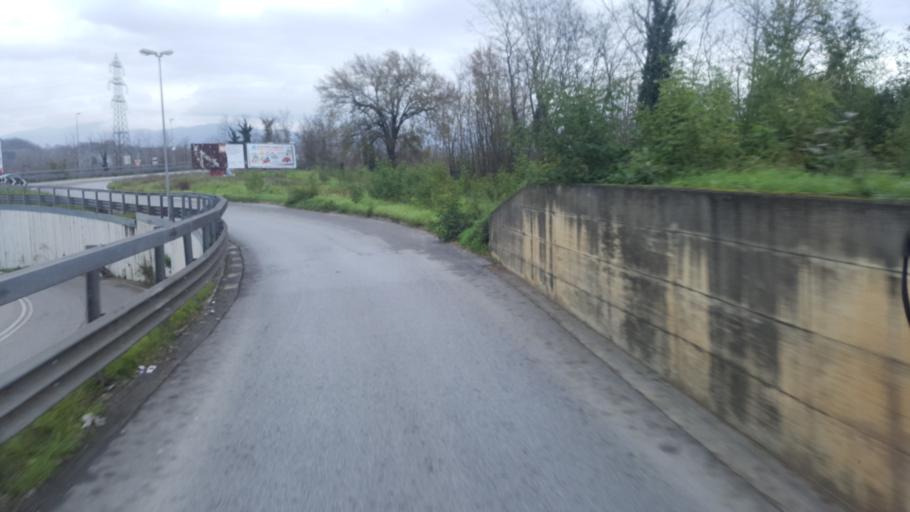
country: IT
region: Tuscany
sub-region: Province of Arezzo
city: Montevarchi
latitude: 43.5388
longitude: 11.5641
